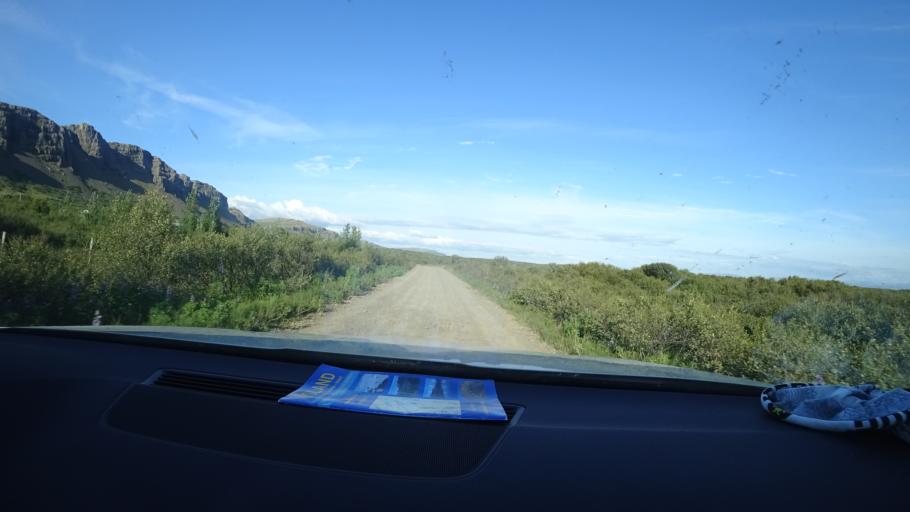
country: IS
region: West
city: Borgarnes
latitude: 64.6920
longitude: -21.9305
